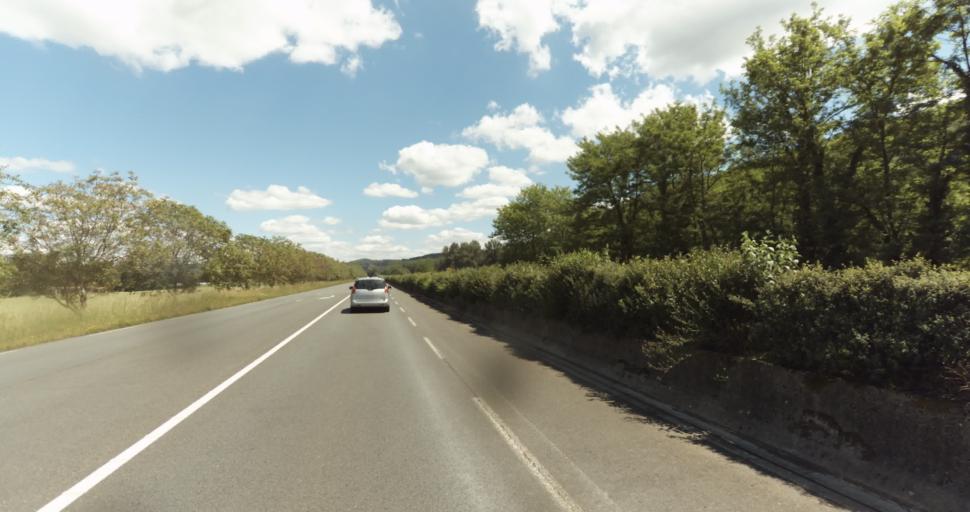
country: FR
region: Aquitaine
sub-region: Departement de la Dordogne
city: Belves
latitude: 44.8248
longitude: 0.9552
